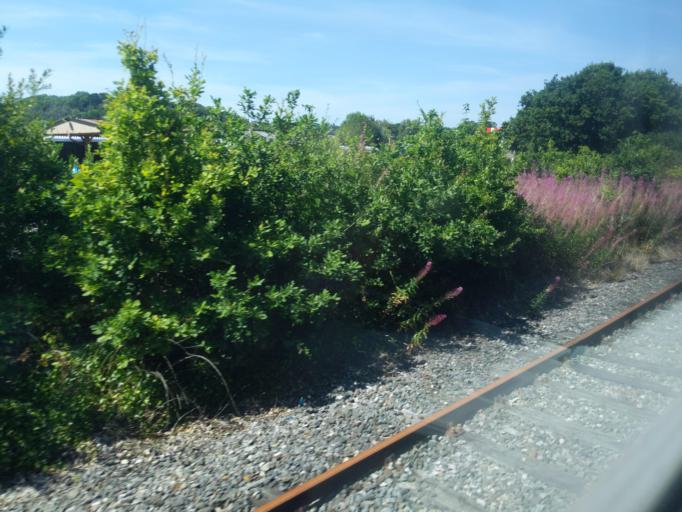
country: GB
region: England
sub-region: Devon
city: Totnes
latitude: 50.4393
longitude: -3.6854
